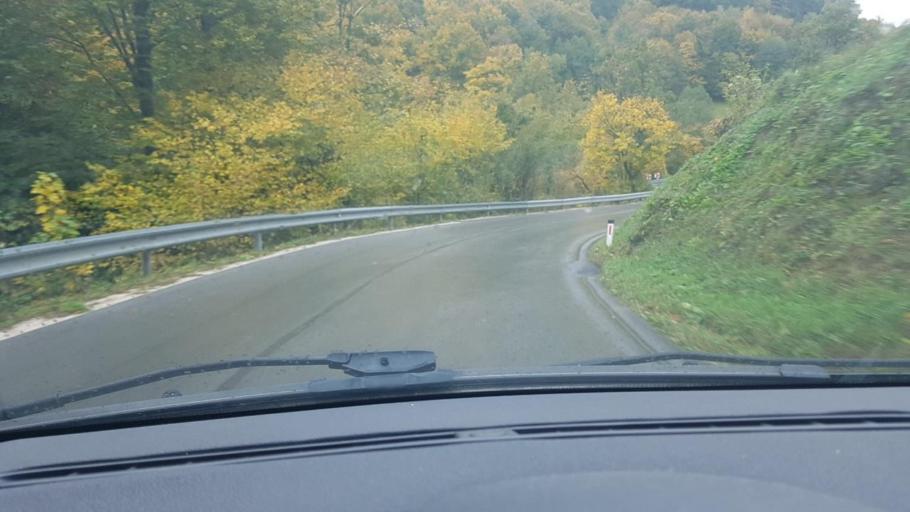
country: SI
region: Rogatec
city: Rogatec
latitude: 46.2642
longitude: 15.7059
